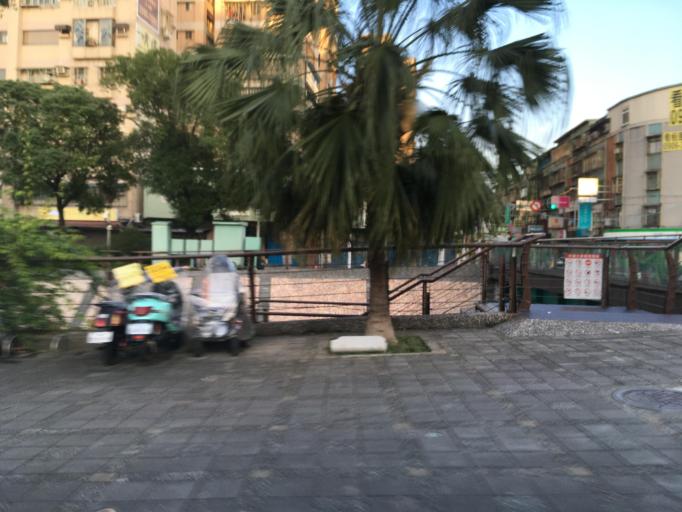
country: TW
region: Taipei
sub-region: Taipei
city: Banqiao
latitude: 25.0483
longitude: 121.4528
